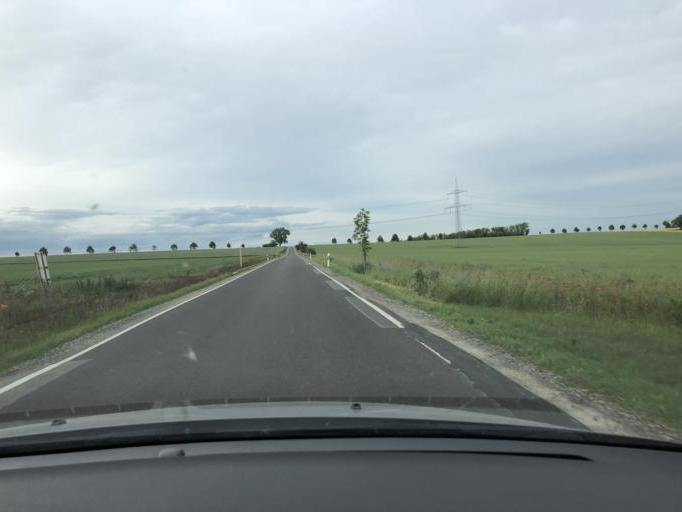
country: DE
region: Thuringia
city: Pfiffelbach
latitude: 51.0690
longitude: 11.4447
